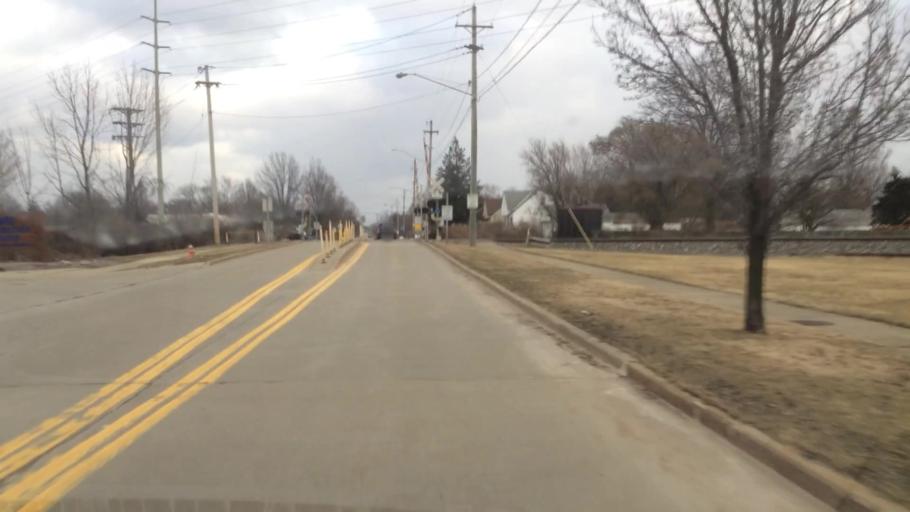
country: US
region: Ohio
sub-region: Cuyahoga County
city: Brook Park
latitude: 41.3950
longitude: -81.8356
